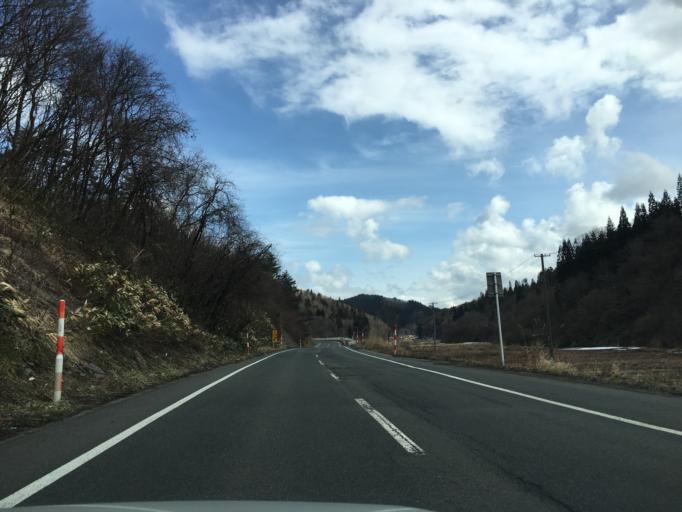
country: JP
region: Akita
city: Odate
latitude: 40.1865
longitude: 140.5080
